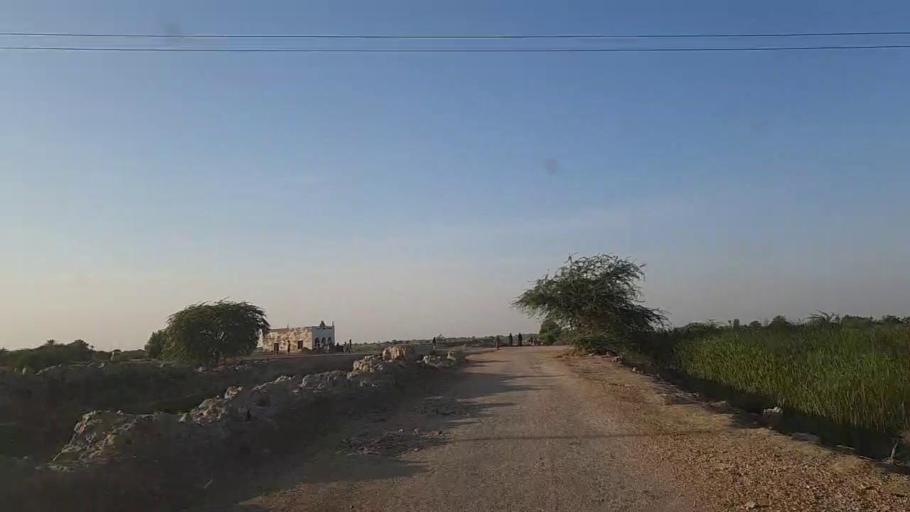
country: PK
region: Sindh
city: Mirpur Batoro
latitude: 24.6979
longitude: 68.2001
